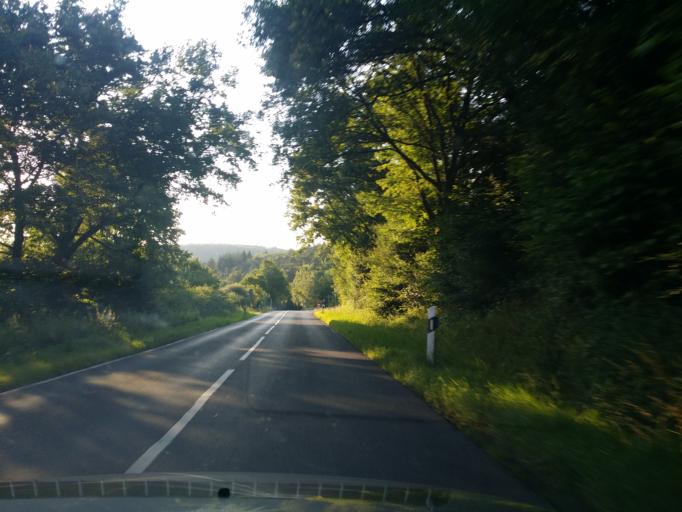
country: DE
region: Hesse
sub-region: Regierungsbezirk Darmstadt
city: Glashutten
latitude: 50.1838
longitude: 8.3643
